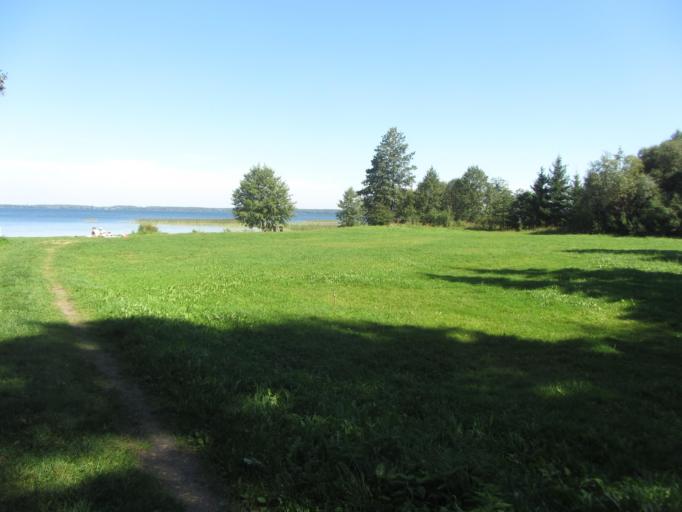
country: LT
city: Simnas
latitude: 54.2624
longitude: 23.6958
